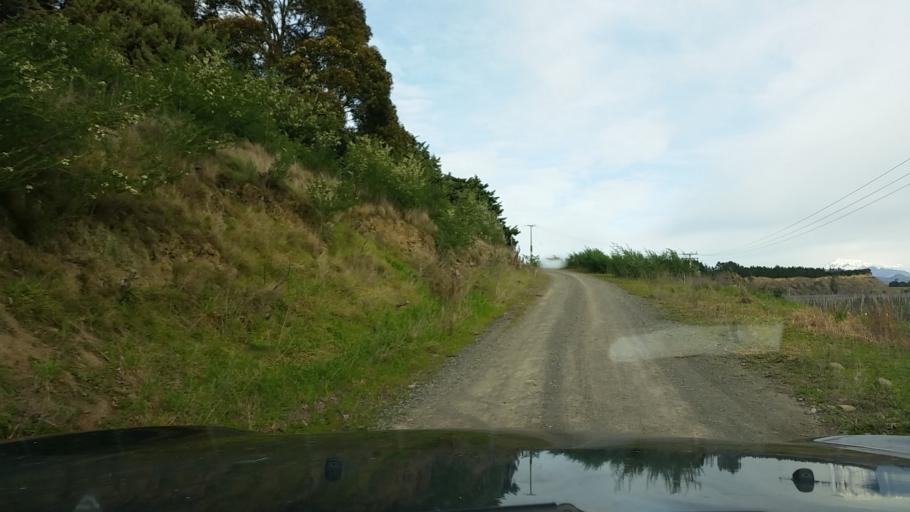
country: NZ
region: Marlborough
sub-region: Marlborough District
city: Blenheim
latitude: -41.6337
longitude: 174.1205
